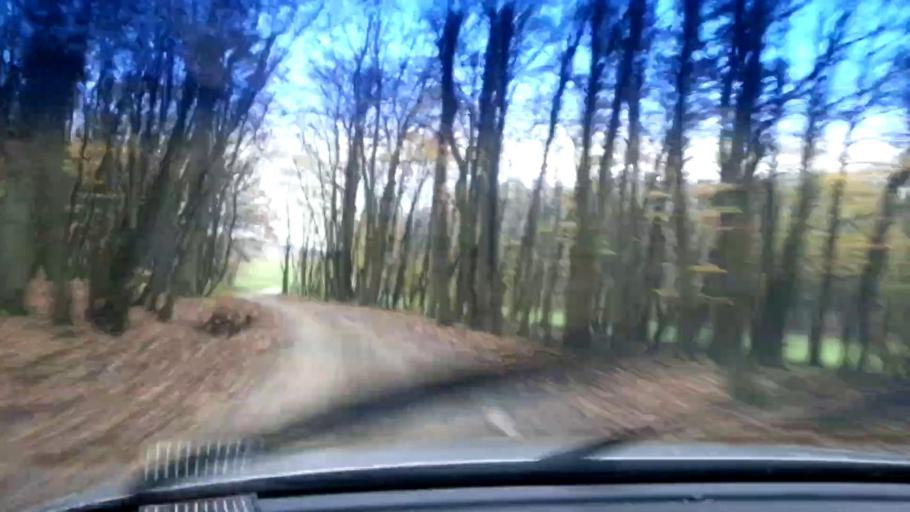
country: DE
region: Bavaria
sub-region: Upper Franconia
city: Litzendorf
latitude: 49.9352
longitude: 11.0018
